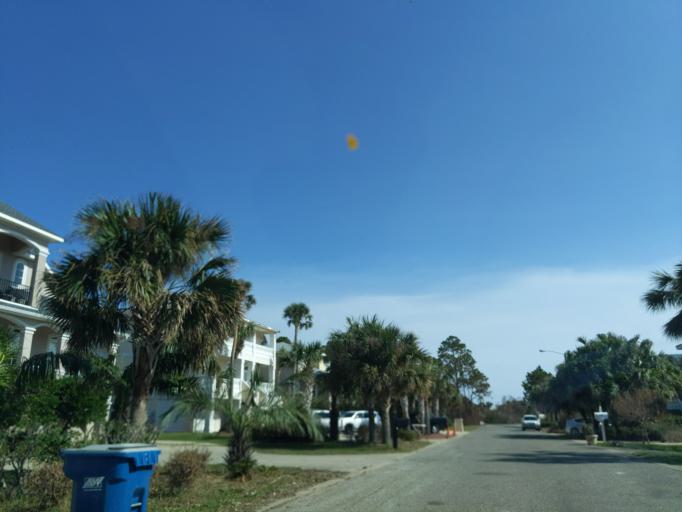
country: US
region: Florida
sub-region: Santa Rosa County
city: Gulf Breeze
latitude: 30.3489
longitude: -87.1871
